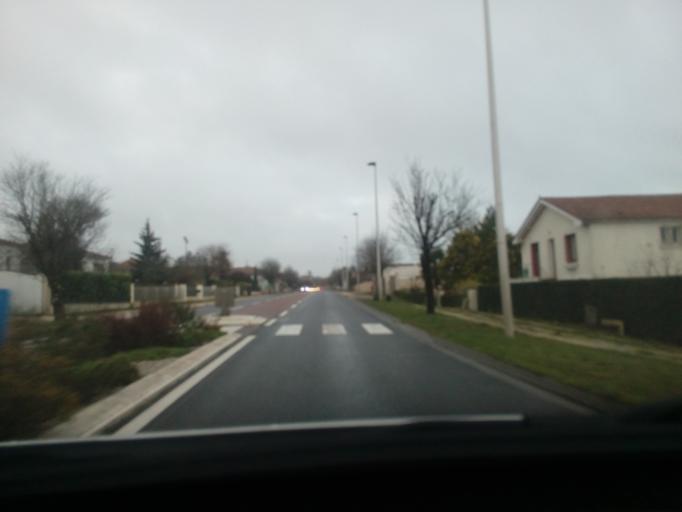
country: FR
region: Poitou-Charentes
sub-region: Departement de la Charente
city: Barbezieux-Saint-Hilaire
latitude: 45.4799
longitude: -0.1449
